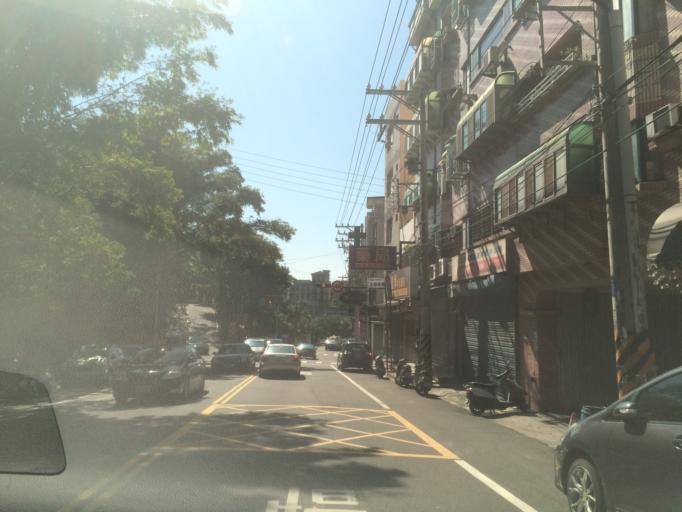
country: TW
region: Taiwan
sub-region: Hsinchu
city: Hsinchu
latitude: 24.7843
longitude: 120.9675
